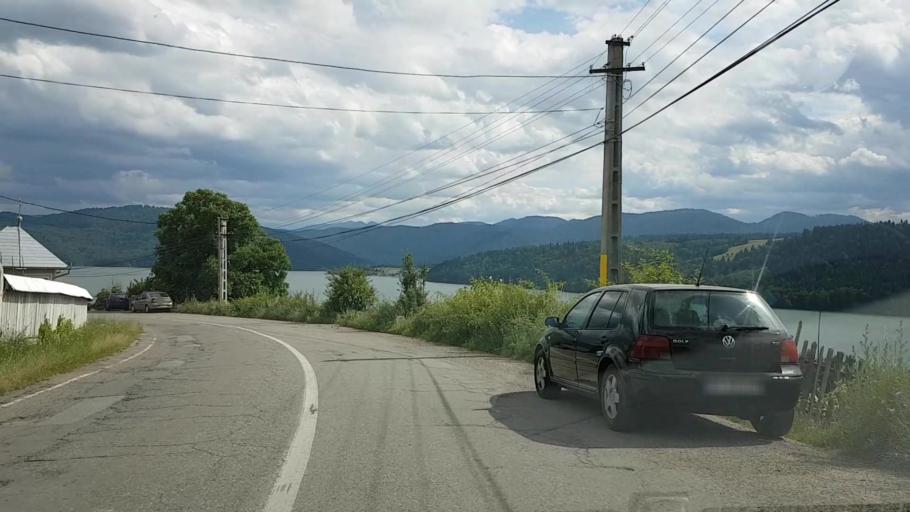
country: RO
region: Neamt
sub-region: Comuna Hangu
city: Hangu
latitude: 47.0188
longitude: 26.0732
